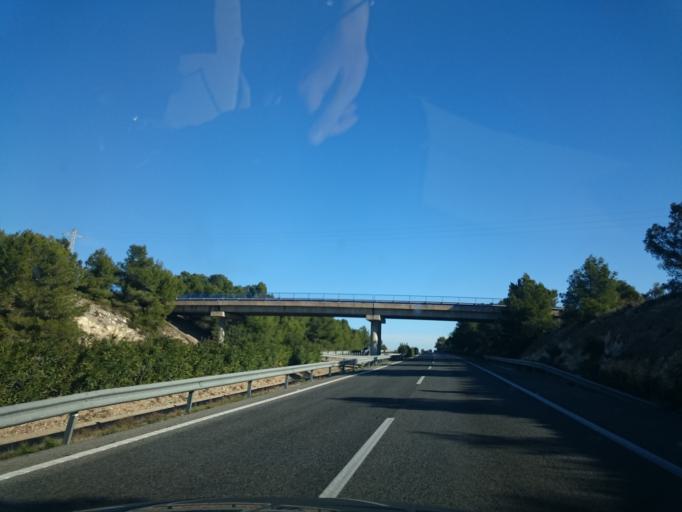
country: ES
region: Catalonia
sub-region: Provincia de Tarragona
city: El Perello
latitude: 40.8499
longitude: 0.7565
